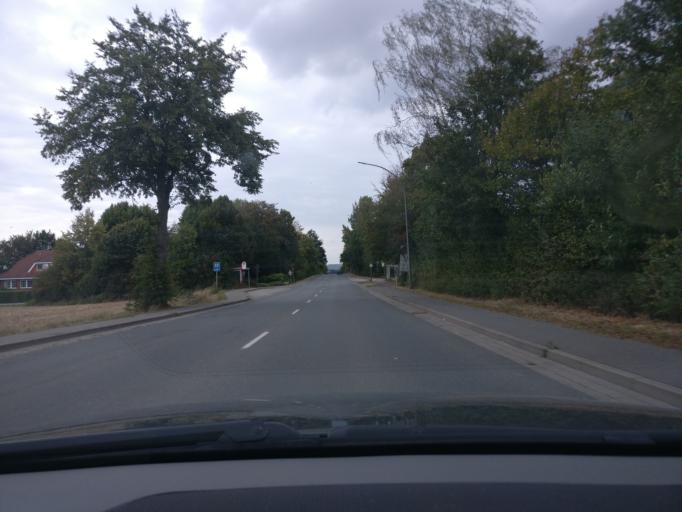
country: DE
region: Lower Saxony
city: Melle
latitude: 52.1906
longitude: 8.3369
